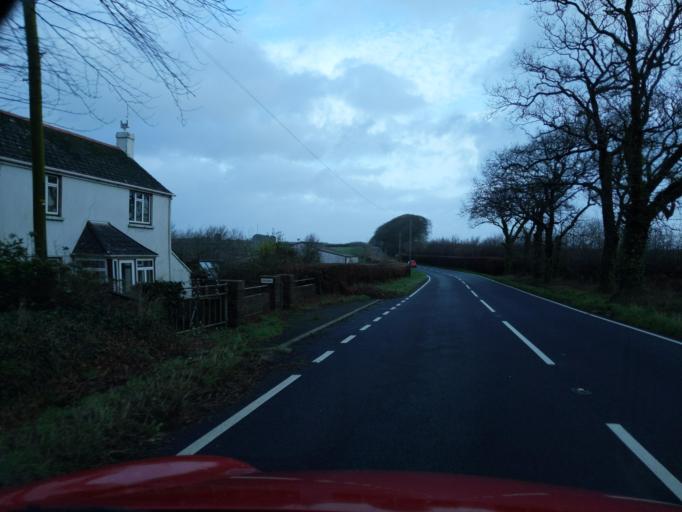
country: GB
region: England
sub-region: Devon
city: Great Torrington
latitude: 50.9062
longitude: -4.2508
